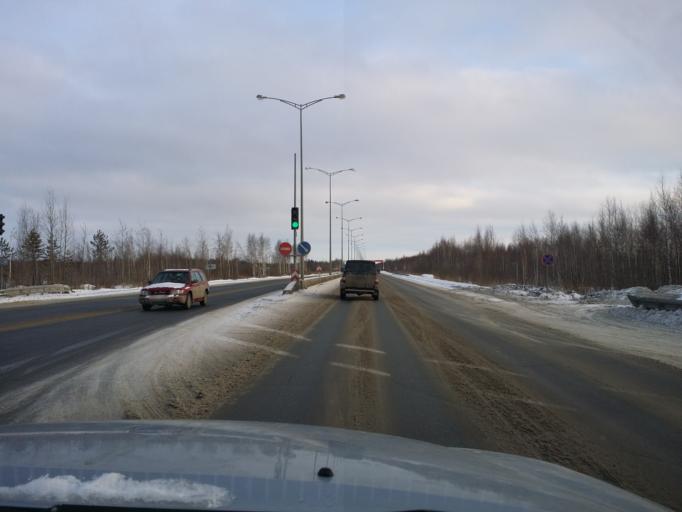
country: RU
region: Khanty-Mansiyskiy Avtonomnyy Okrug
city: Nizhnevartovsk
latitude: 60.9846
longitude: 76.4795
